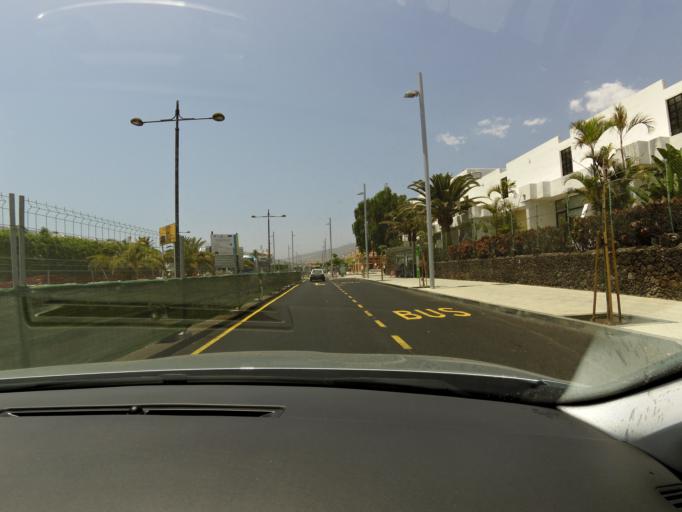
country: ES
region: Canary Islands
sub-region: Provincia de Santa Cruz de Tenerife
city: Playa de las Americas
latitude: 28.0761
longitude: -16.7317
